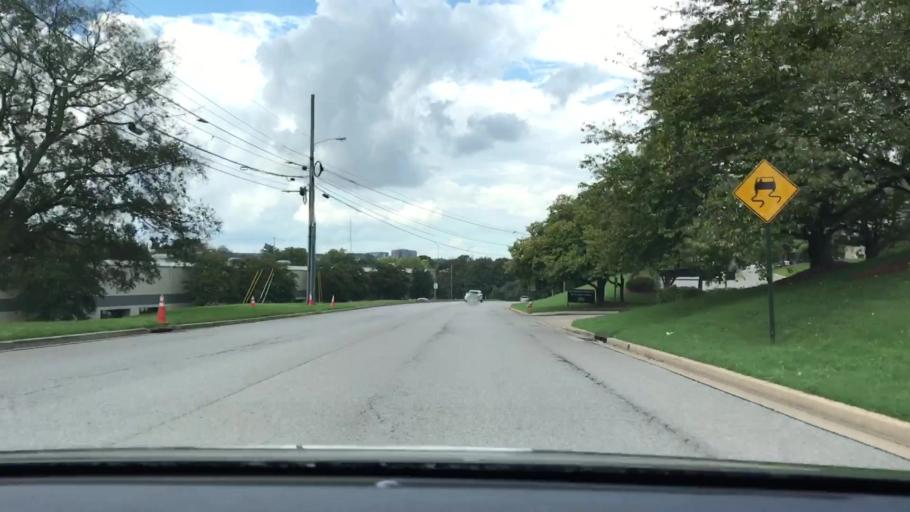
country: US
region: Tennessee
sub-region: Davidson County
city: Oak Hill
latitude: 36.1195
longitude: -86.7611
